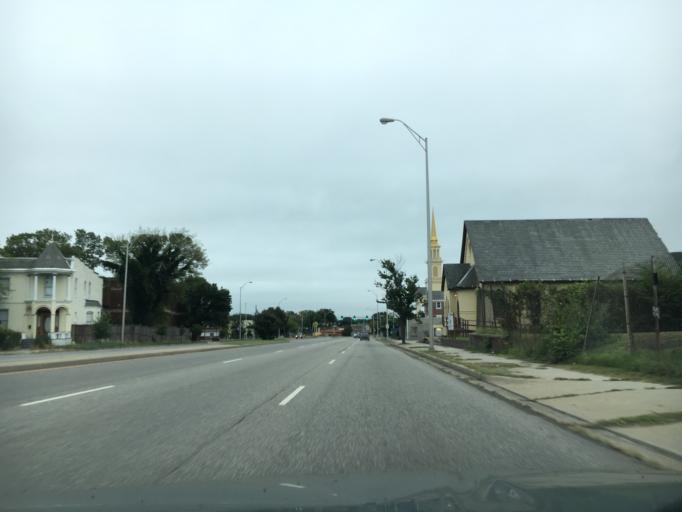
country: US
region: Virginia
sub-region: City of Richmond
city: Richmond
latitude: 37.5206
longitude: -77.4502
